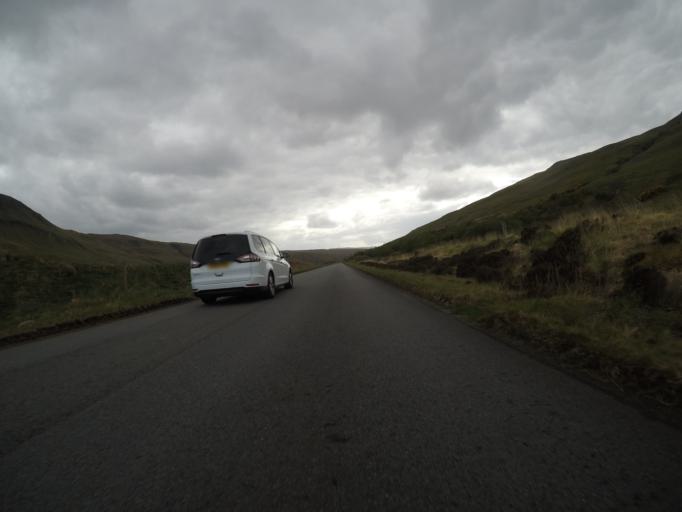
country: GB
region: Scotland
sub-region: Highland
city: Isle of Skye
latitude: 57.3013
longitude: -6.2519
